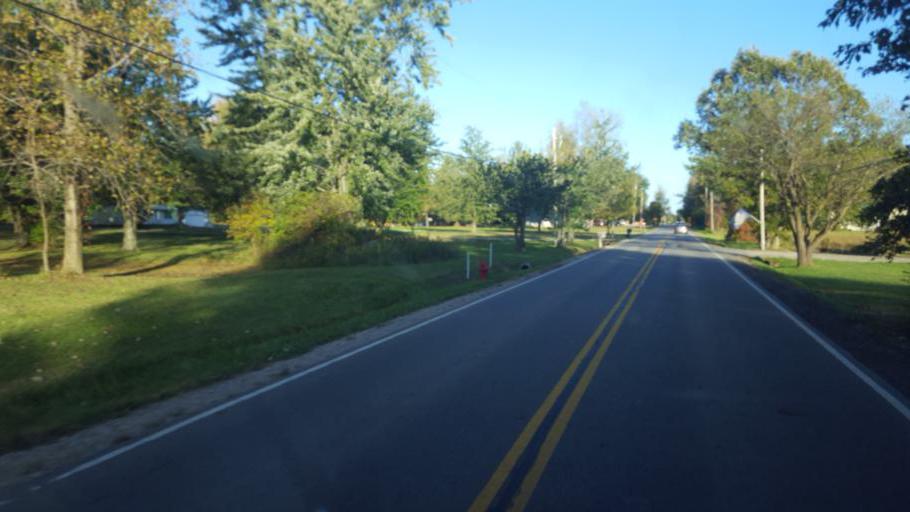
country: US
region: Ohio
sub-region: Licking County
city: Pataskala
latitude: 40.0162
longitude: -82.7545
